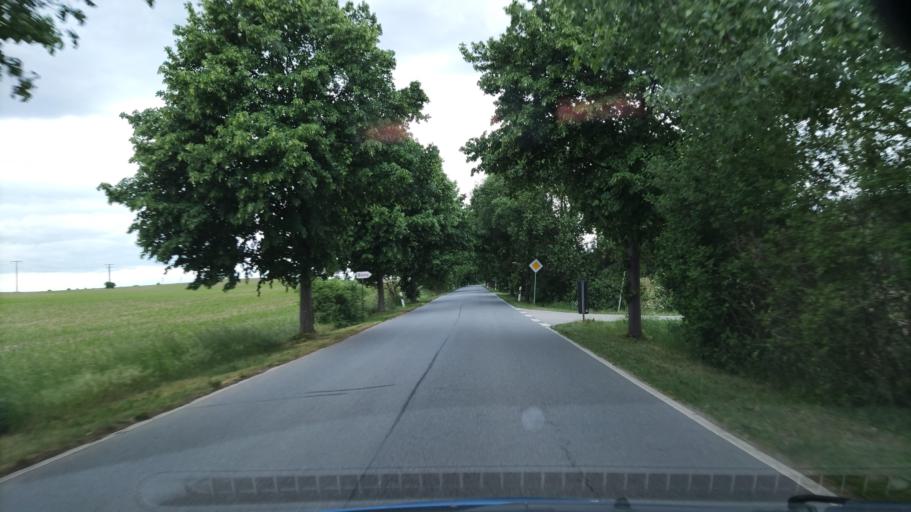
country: DE
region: Mecklenburg-Vorpommern
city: Plau am See
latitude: 53.4554
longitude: 12.2497
